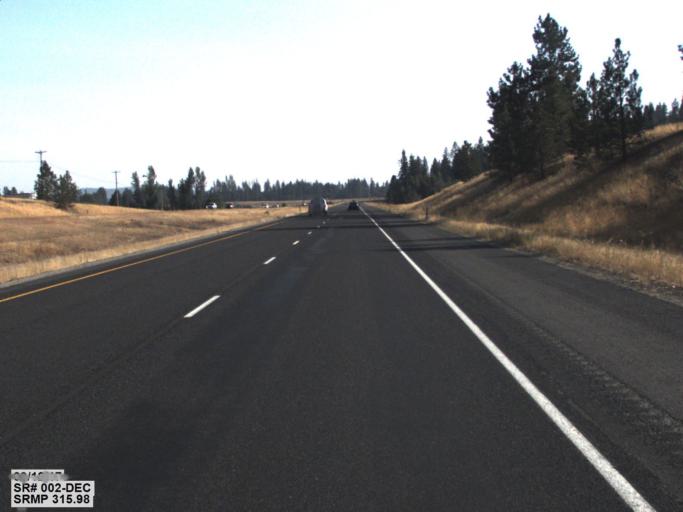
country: US
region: Washington
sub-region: Spokane County
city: Deer Park
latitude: 48.0540
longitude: -117.3444
